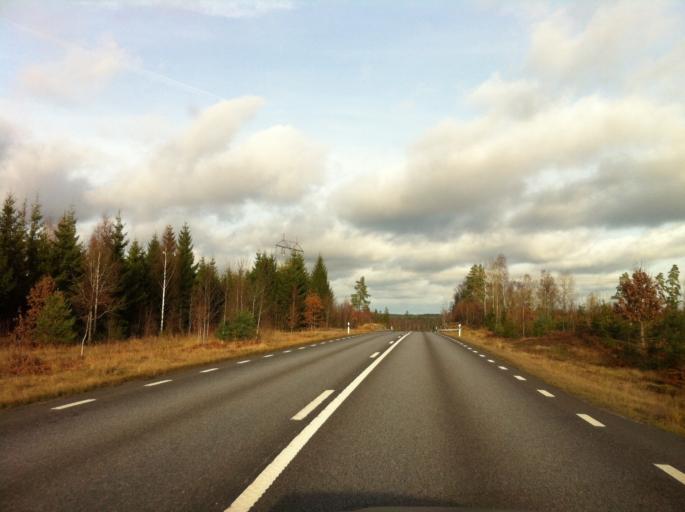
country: SE
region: Kronoberg
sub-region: Vaxjo Kommun
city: Gemla
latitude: 56.7794
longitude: 14.5718
